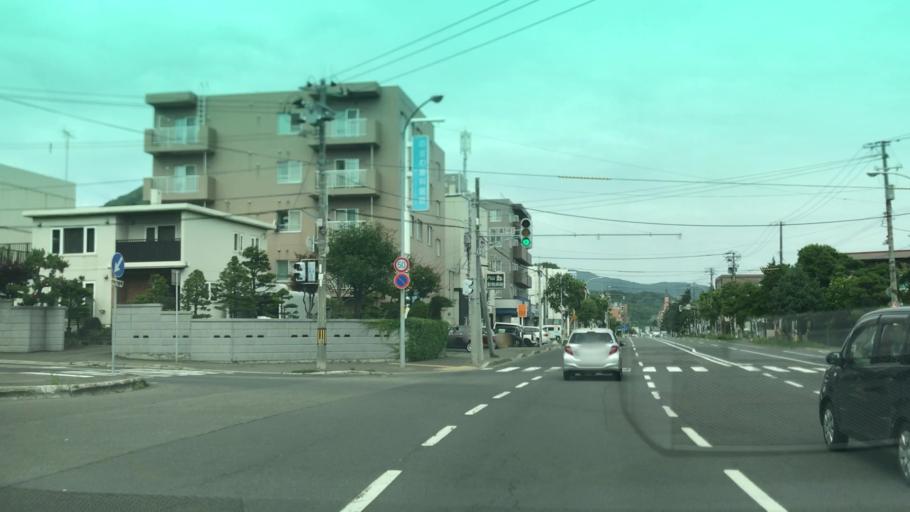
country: JP
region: Hokkaido
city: Sapporo
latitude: 43.0559
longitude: 141.3055
